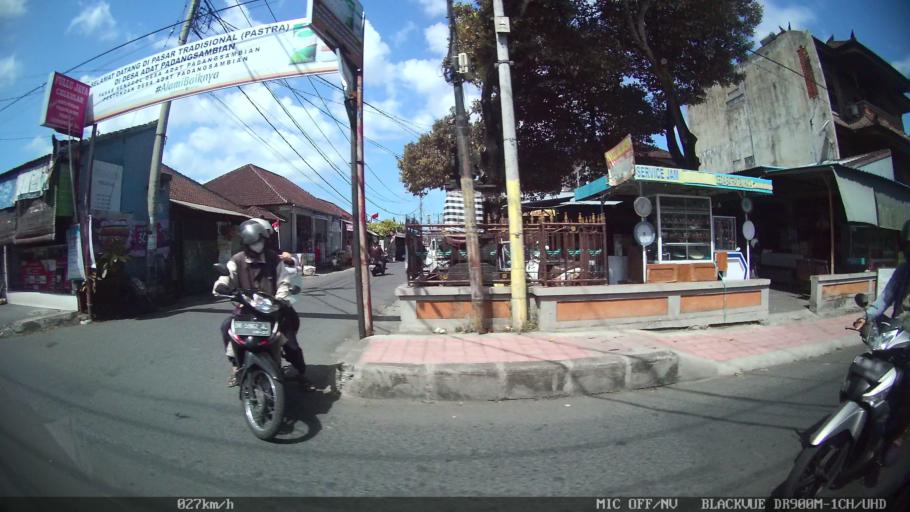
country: ID
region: Bali
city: Denpasar
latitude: -8.6546
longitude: 115.1863
